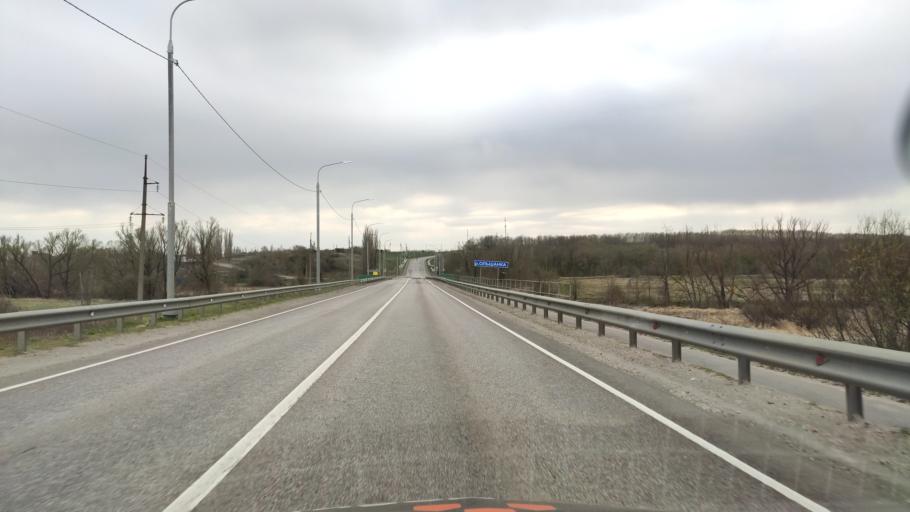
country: RU
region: Voronezj
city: Nizhnedevitsk
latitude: 51.5698
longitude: 38.4737
